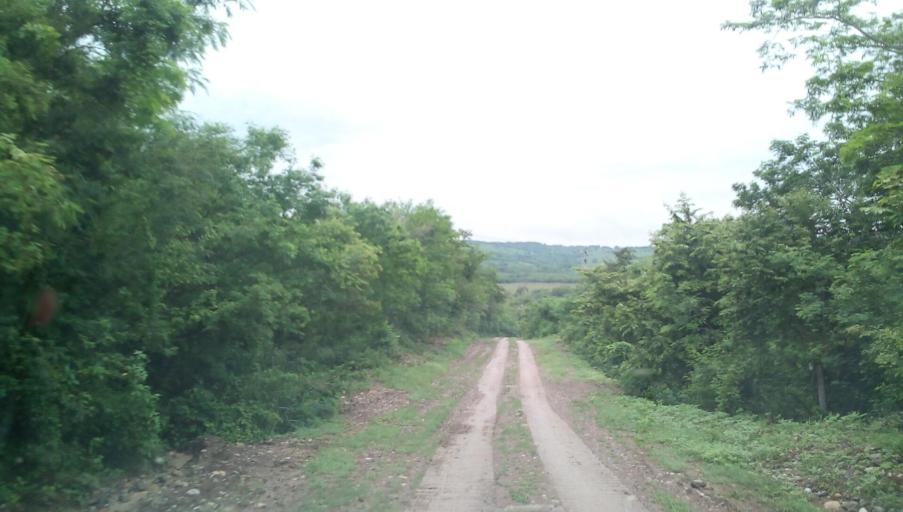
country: MX
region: Veracruz
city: Tempoal de Sanchez
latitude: 21.4326
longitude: -98.4190
